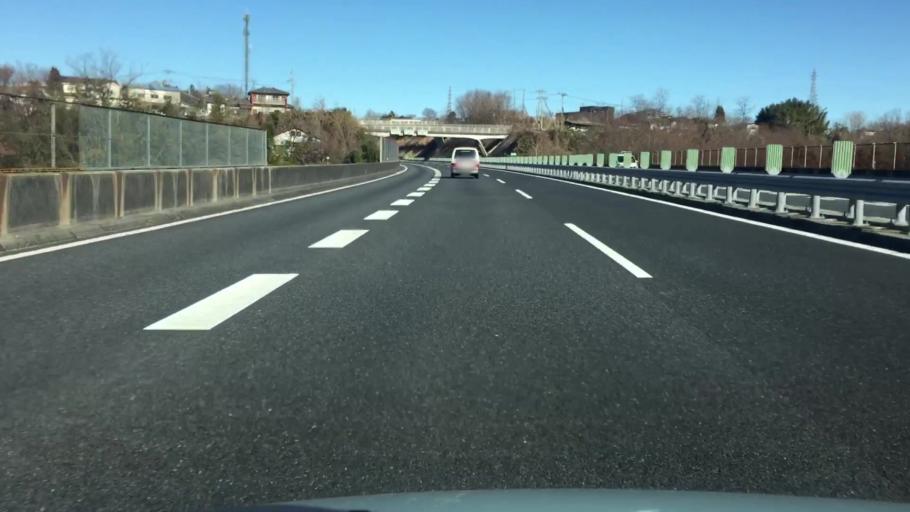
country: JP
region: Gunma
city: Shibukawa
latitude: 36.4906
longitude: 139.0309
